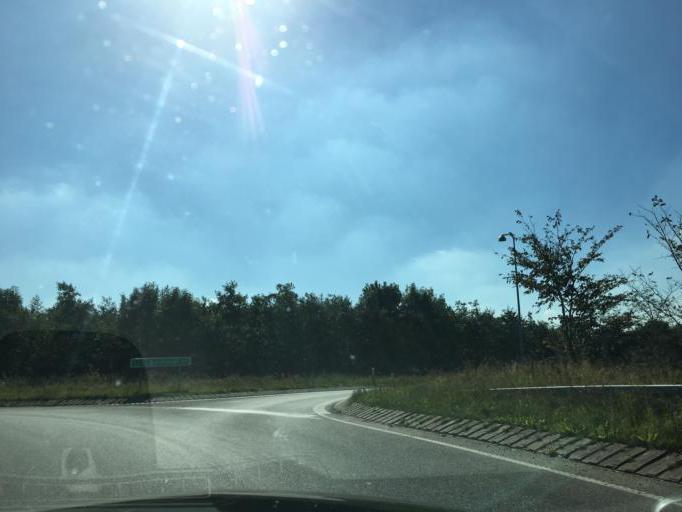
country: DK
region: South Denmark
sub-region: Kolding Kommune
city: Lunderskov
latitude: 55.5048
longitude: 9.2758
